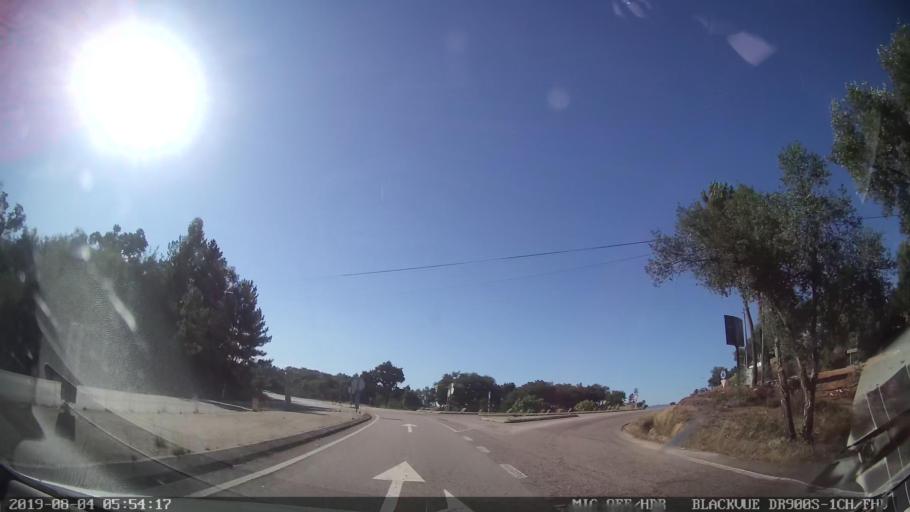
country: PT
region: Portalegre
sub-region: Gaviao
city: Gaviao
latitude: 39.4632
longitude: -7.9417
